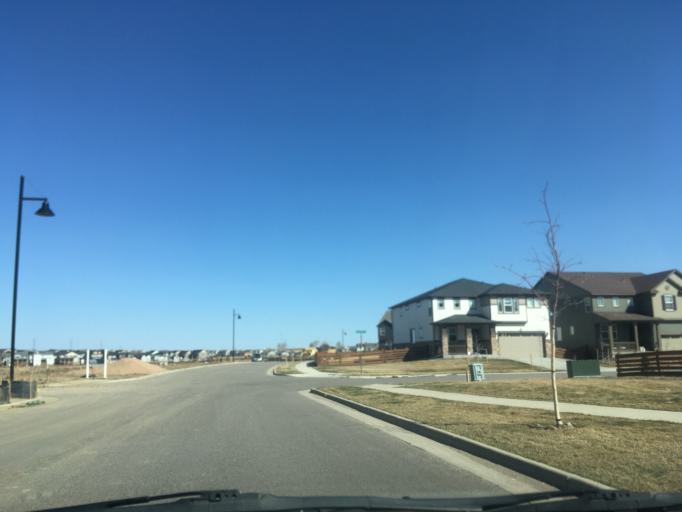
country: US
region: Colorado
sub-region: Boulder County
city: Erie
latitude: 40.0546
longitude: -105.0360
